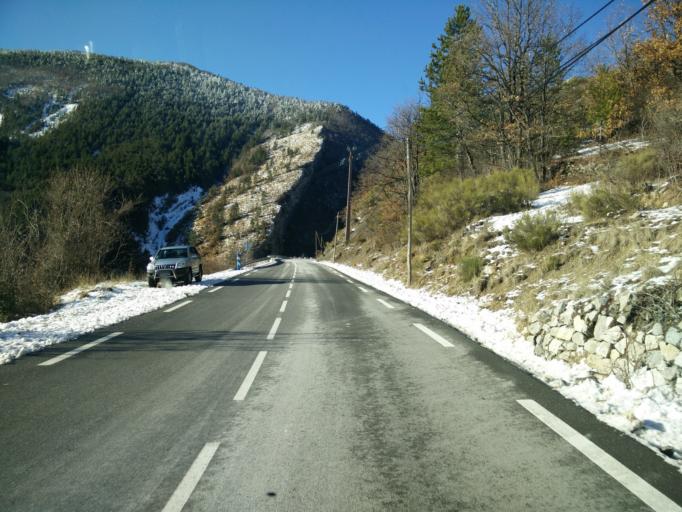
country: FR
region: Provence-Alpes-Cote d'Azur
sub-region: Departement des Alpes-de-Haute-Provence
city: Annot
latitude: 43.9317
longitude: 6.6621
